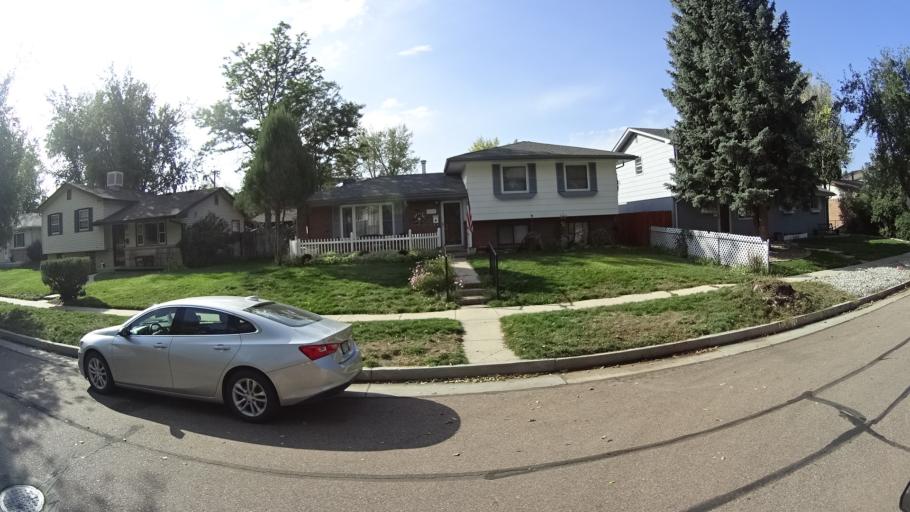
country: US
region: Colorado
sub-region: El Paso County
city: Colorado Springs
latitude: 38.8560
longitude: -104.7837
